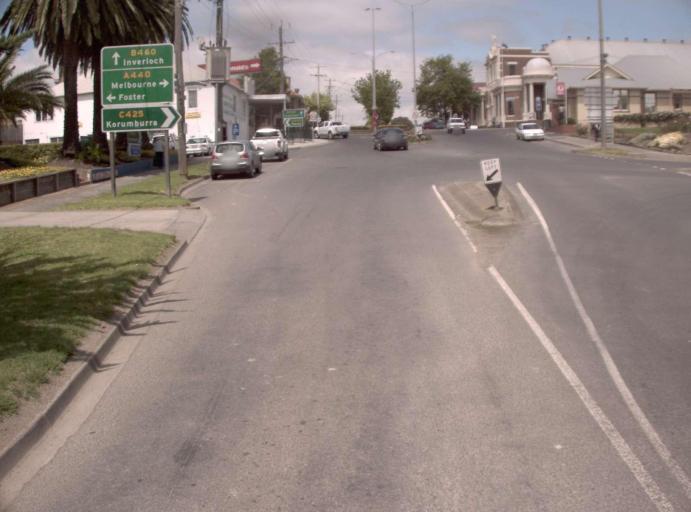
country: AU
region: Victoria
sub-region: Baw Baw
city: Warragul
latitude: -38.4757
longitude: 145.9472
